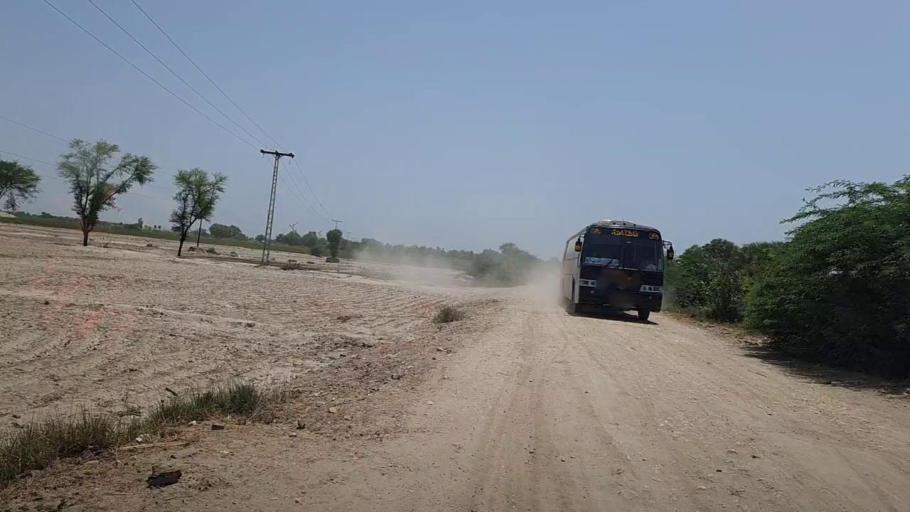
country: PK
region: Sindh
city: Pad Idan
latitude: 26.7623
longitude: 68.2936
